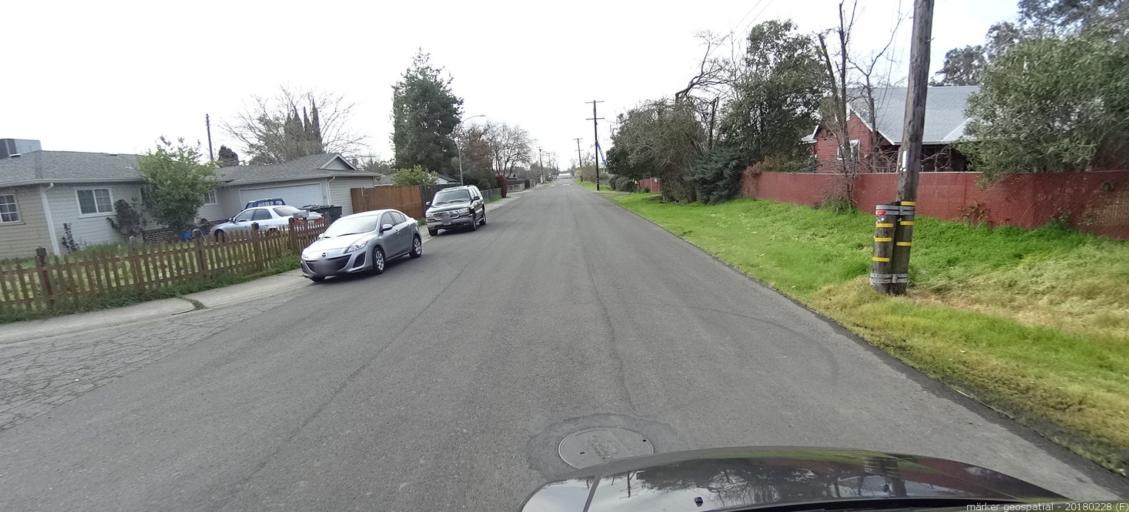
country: US
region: California
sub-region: Sacramento County
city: Rio Linda
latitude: 38.6963
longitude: -121.4500
